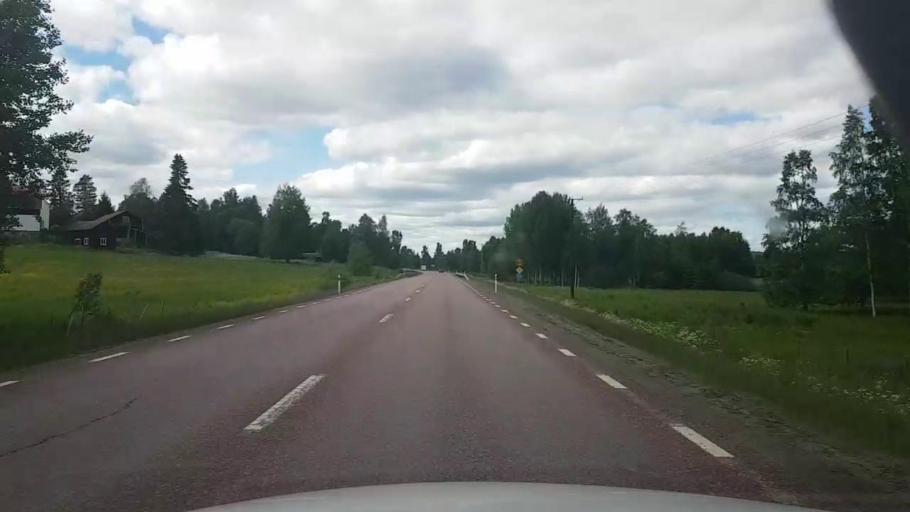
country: SE
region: Gaevleborg
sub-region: Ljusdals Kommun
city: Ljusdal
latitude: 61.8111
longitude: 16.0914
